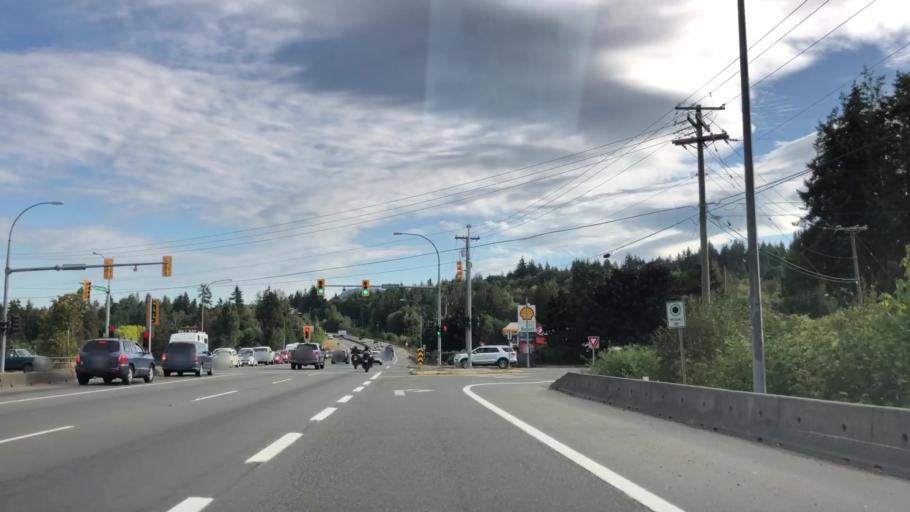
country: CA
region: British Columbia
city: North Saanich
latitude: 48.6531
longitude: -123.5604
